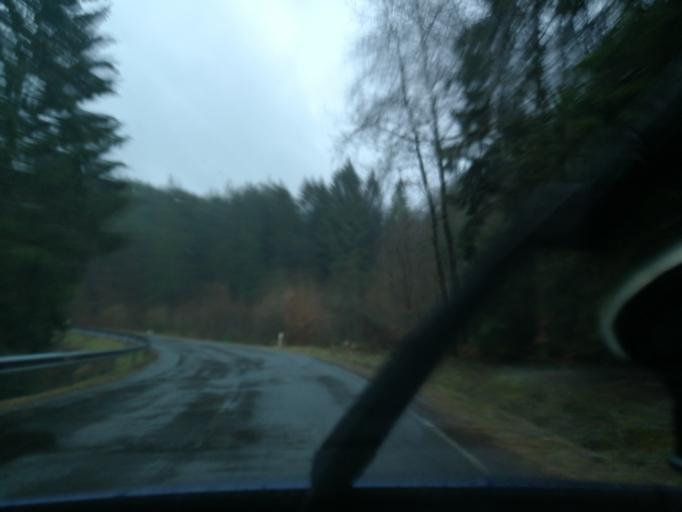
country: DE
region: Rheinland-Pfalz
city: Gielert
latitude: 49.7750
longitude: 6.9944
